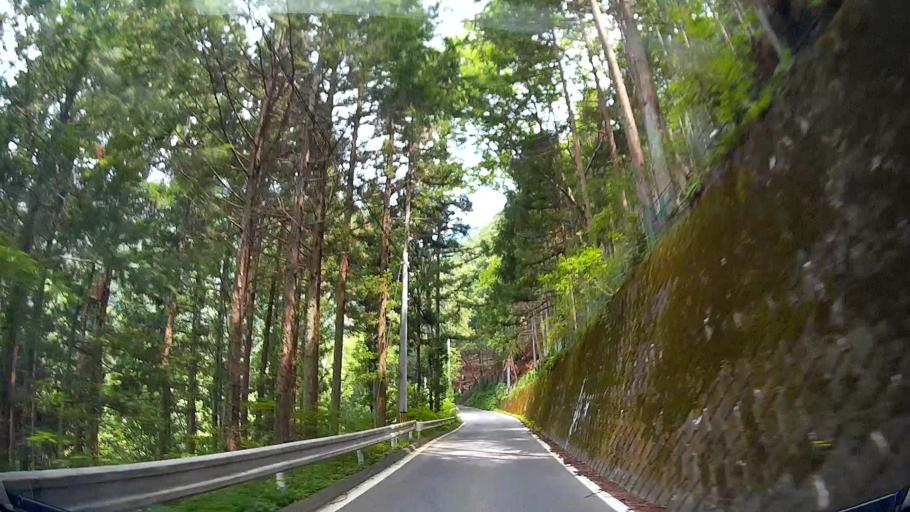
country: JP
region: Nagano
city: Iida
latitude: 35.3261
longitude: 137.9495
